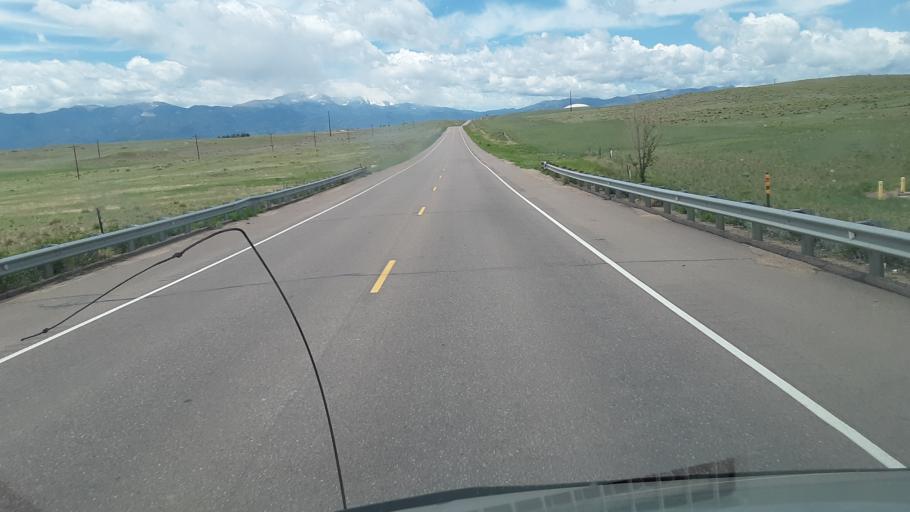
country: US
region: Colorado
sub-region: El Paso County
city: Cimarron Hills
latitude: 38.8363
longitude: -104.6528
